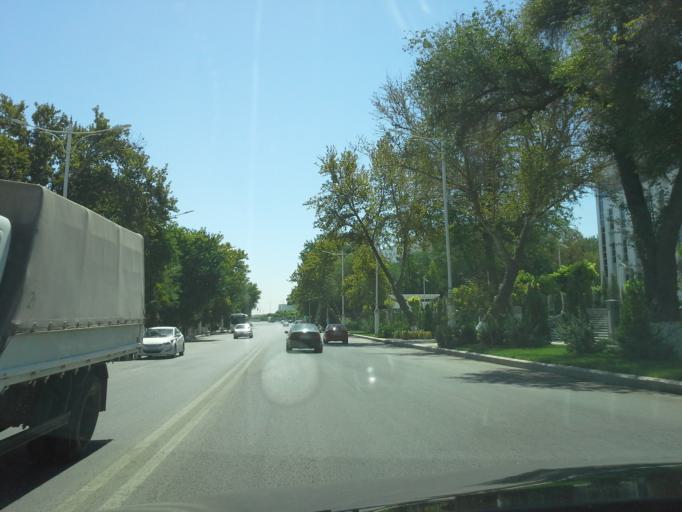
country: TM
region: Ahal
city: Ashgabat
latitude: 37.9443
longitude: 58.3574
